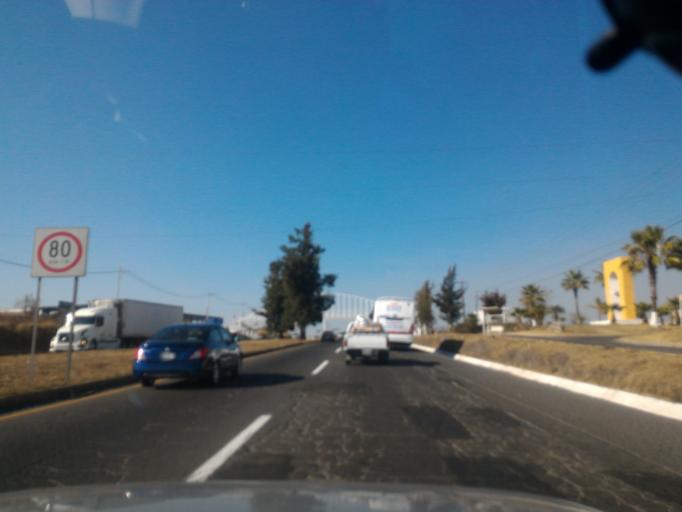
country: MX
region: Jalisco
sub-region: Ixtlahuacan de los Membrillos
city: Los Olivos
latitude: 20.4291
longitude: -103.2395
